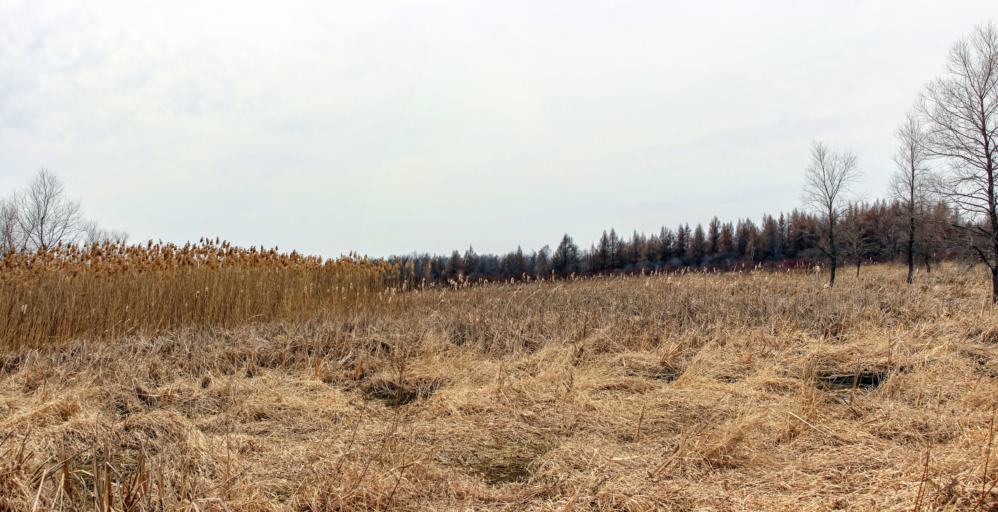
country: US
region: Wisconsin
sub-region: Jefferson County
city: Jefferson
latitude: 42.9789
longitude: -88.7465
